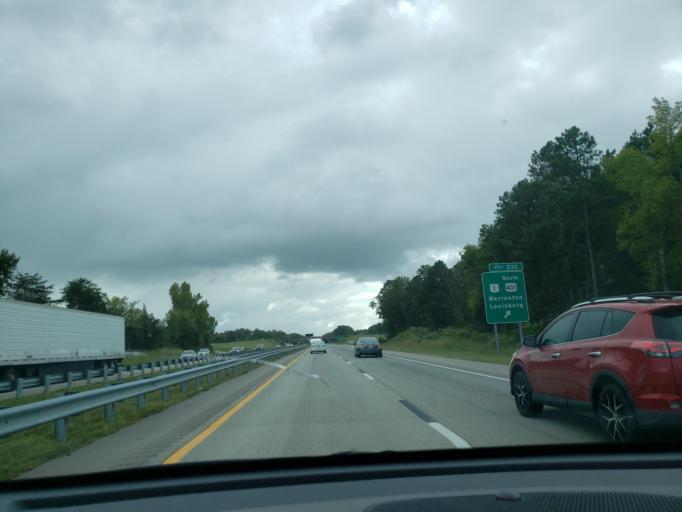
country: US
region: Virginia
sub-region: Mecklenburg County
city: Bracey
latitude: 36.5381
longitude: -78.1886
